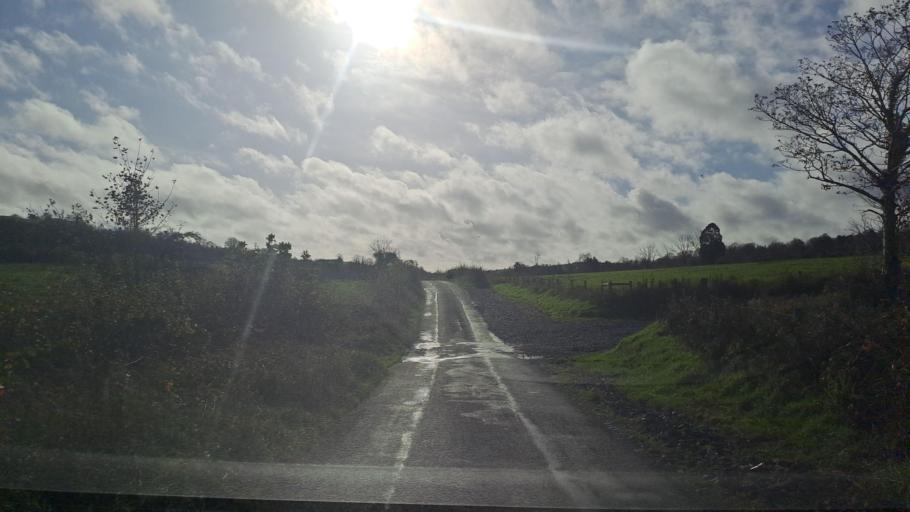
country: IE
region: Ulster
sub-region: An Cabhan
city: Cootehill
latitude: 54.0144
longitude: -7.0374
